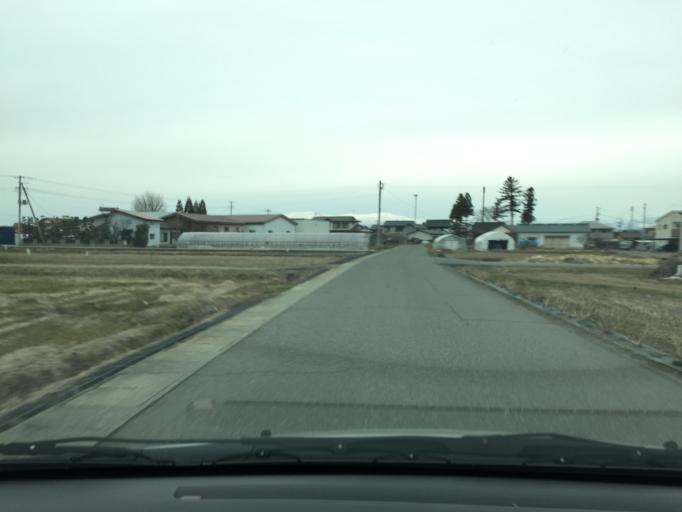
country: JP
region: Fukushima
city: Kitakata
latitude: 37.5145
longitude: 139.8753
